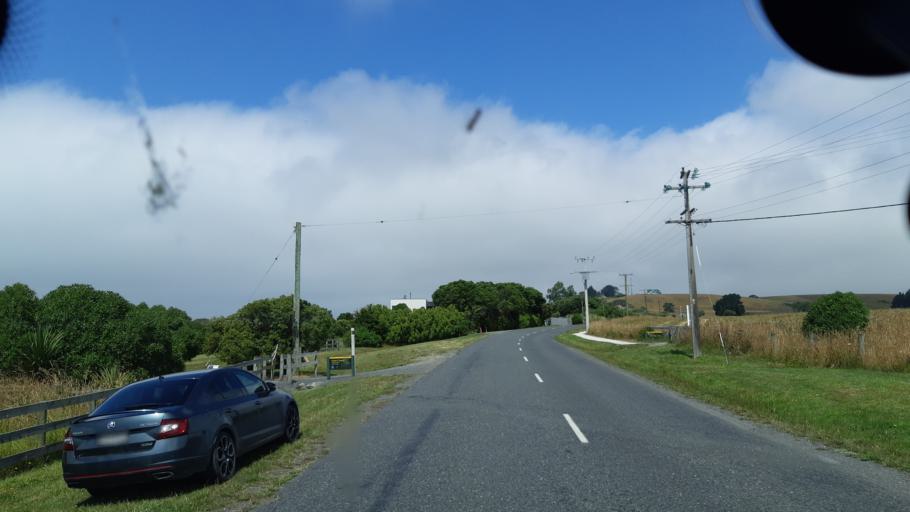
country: NZ
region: Canterbury
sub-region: Kaikoura District
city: Kaikoura
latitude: -42.4124
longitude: 173.6828
